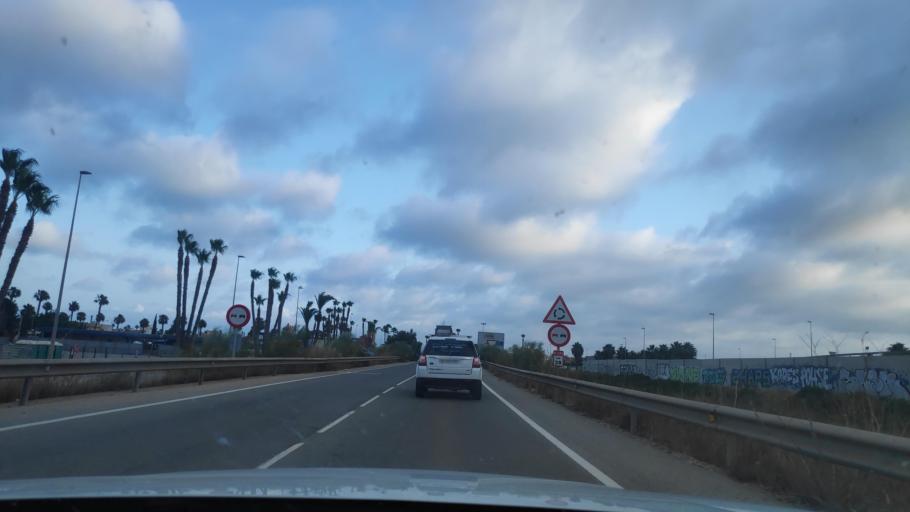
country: ES
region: Murcia
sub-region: Murcia
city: Los Alcazares
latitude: 37.7686
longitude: -0.8437
